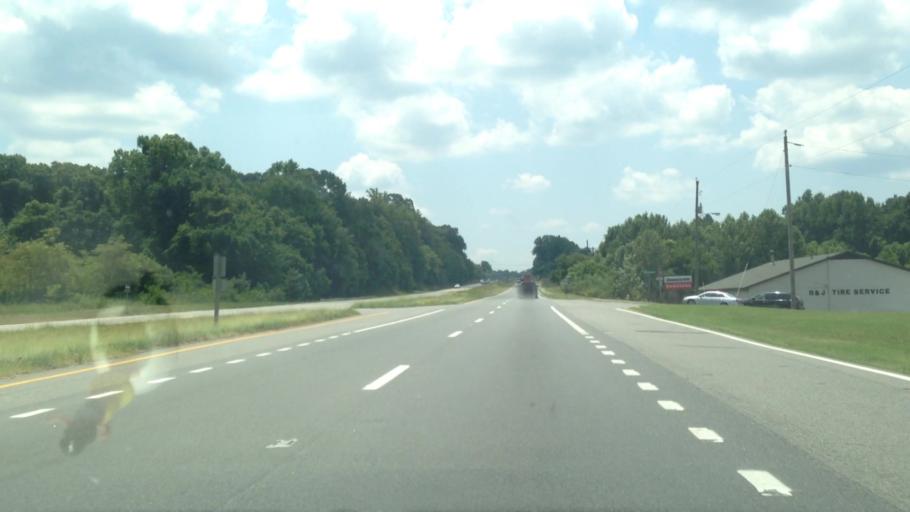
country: US
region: Virginia
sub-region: Henry County
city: Chatmoss
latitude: 36.5947
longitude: -79.8628
